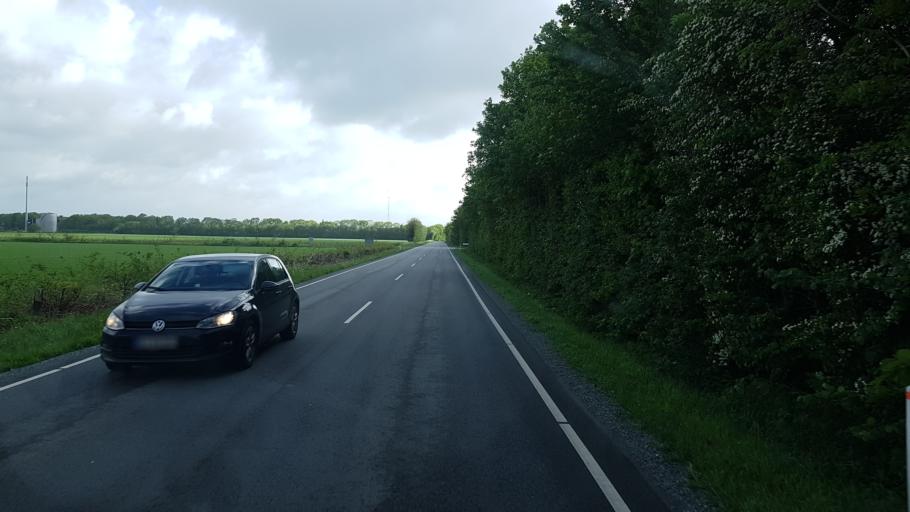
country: DK
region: South Denmark
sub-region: Vejen Kommune
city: Vejen
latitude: 55.4623
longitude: 9.1699
